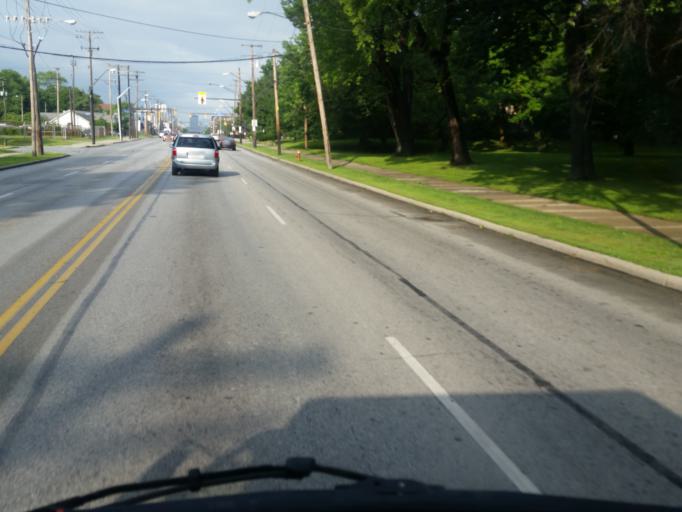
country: US
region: Ohio
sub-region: Cuyahoga County
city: Bratenahl
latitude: 41.5322
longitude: -81.6301
